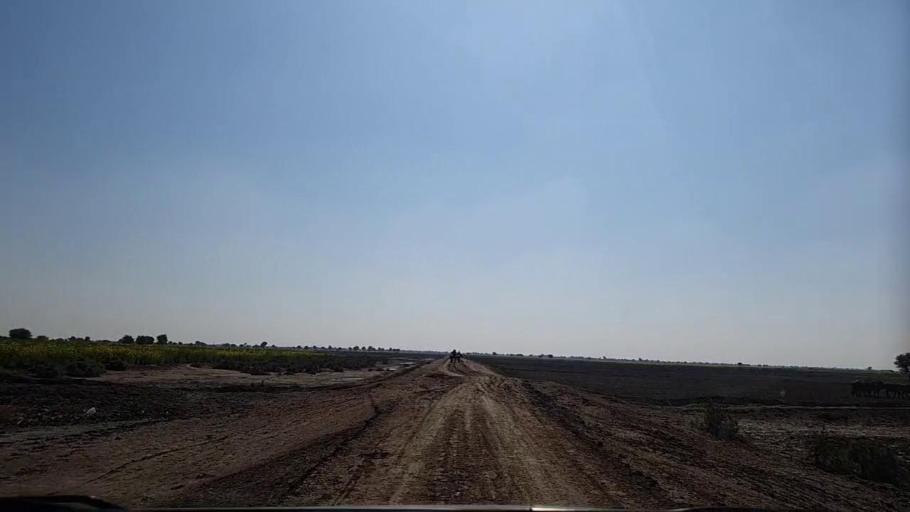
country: PK
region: Sindh
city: Pithoro
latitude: 25.6888
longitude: 69.3557
